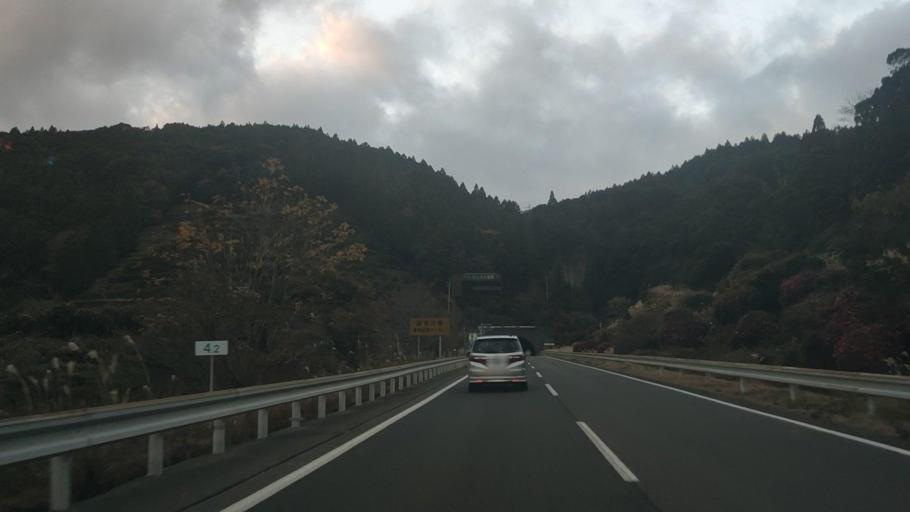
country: JP
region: Nagasaki
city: Obita
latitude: 32.8118
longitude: 129.9325
